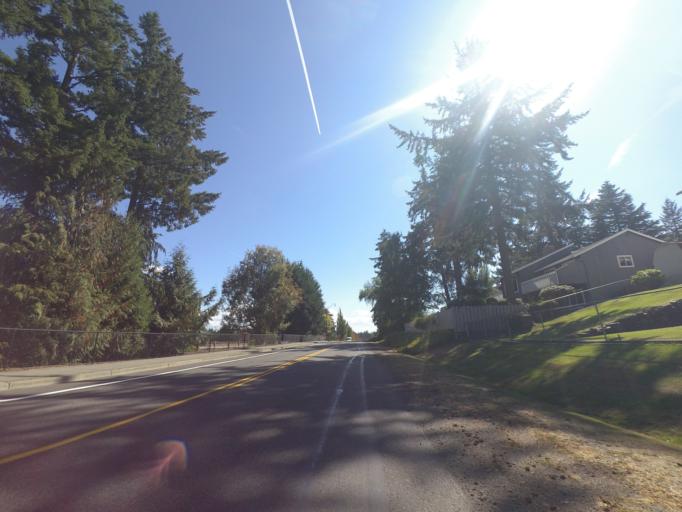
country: US
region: Washington
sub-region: Pierce County
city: Fircrest
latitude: 47.2115
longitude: -122.5160
